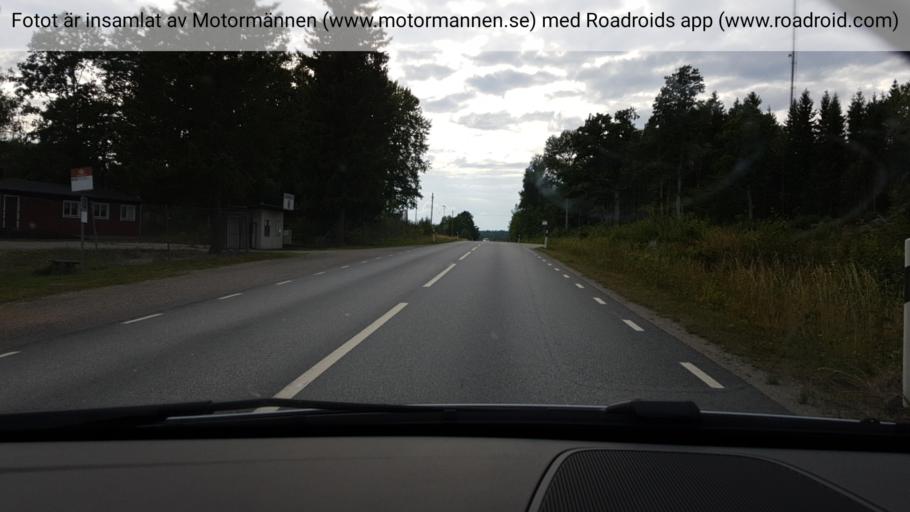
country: SE
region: Stockholm
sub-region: Norrtalje Kommun
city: Skanninge
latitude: 59.8949
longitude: 18.4519
